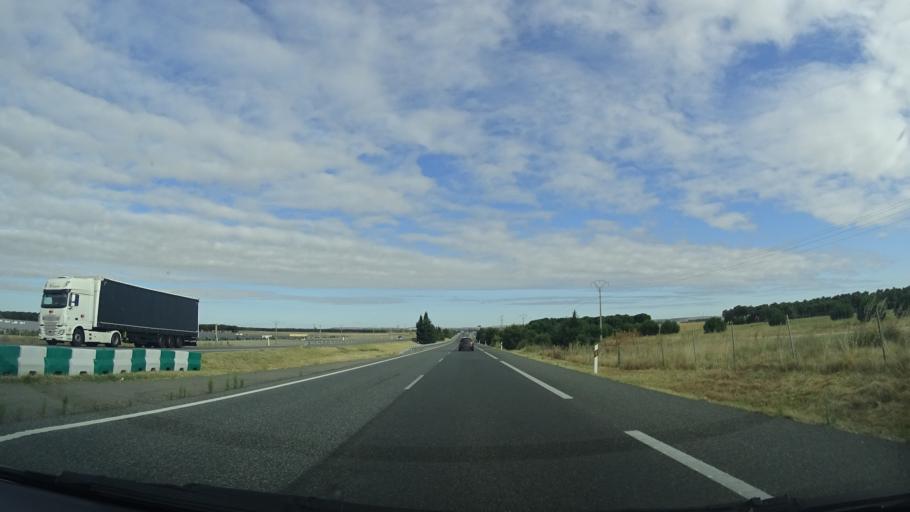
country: ES
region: Castille and Leon
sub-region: Provincia de Valladolid
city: San Vicente del Palacio
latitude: 41.2600
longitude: -4.8774
